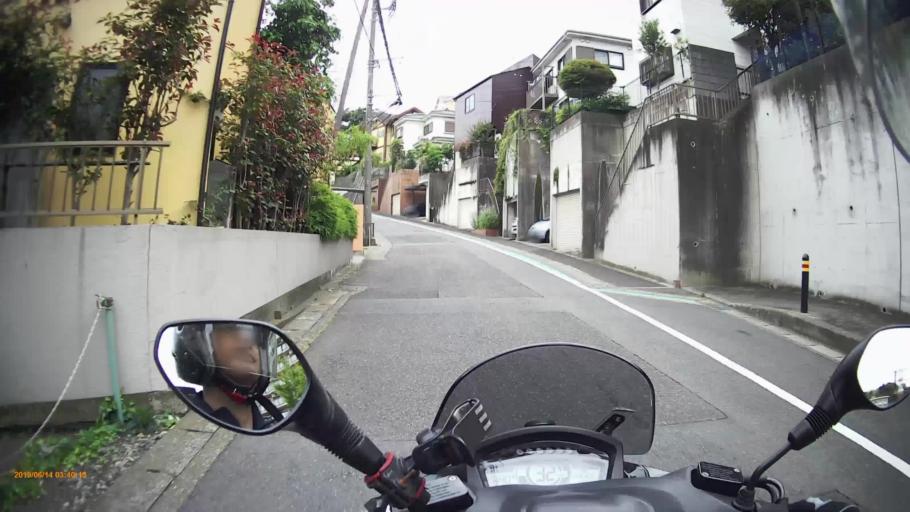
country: JP
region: Kanagawa
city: Minami-rinkan
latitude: 35.4167
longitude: 139.4464
